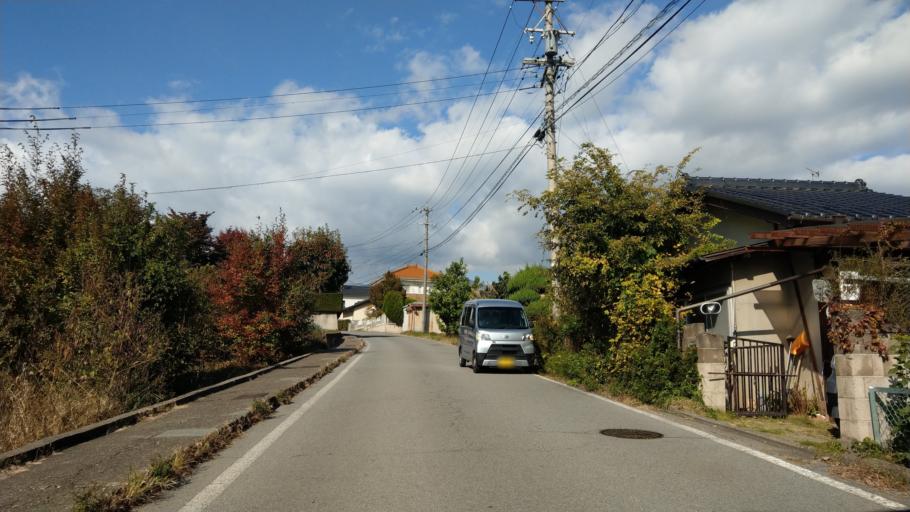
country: JP
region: Nagano
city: Komoro
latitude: 36.3151
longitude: 138.4410
